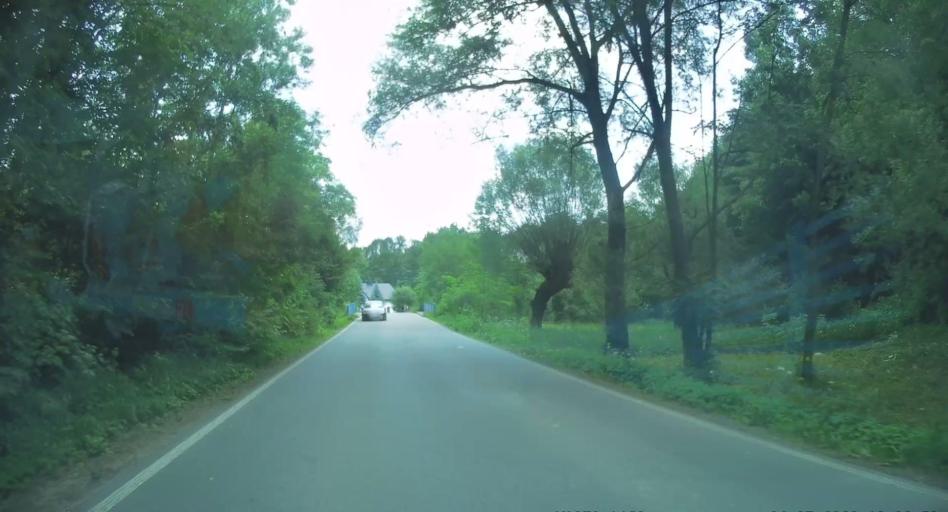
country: PL
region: Lesser Poland Voivodeship
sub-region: Powiat nowosadecki
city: Korzenna
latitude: 49.7232
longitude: 20.7742
